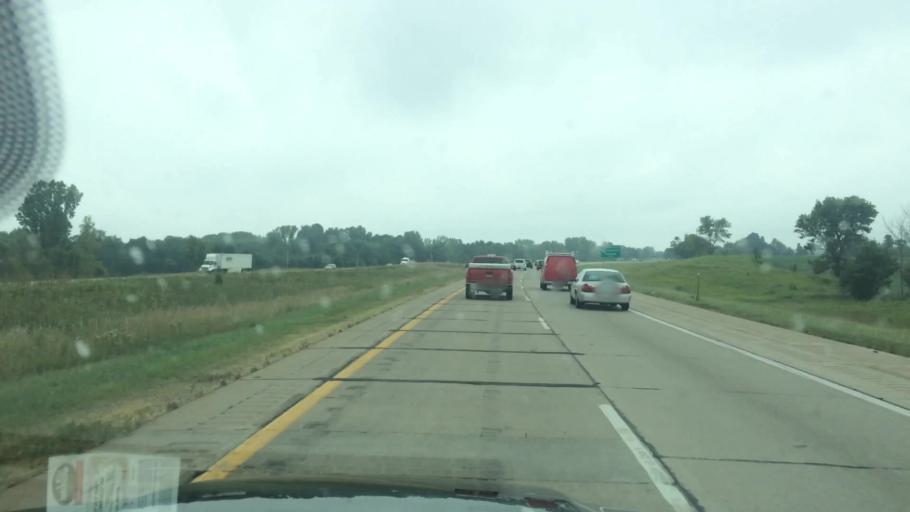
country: US
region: Michigan
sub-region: Eaton County
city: Charlotte
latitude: 42.5007
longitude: -84.8593
